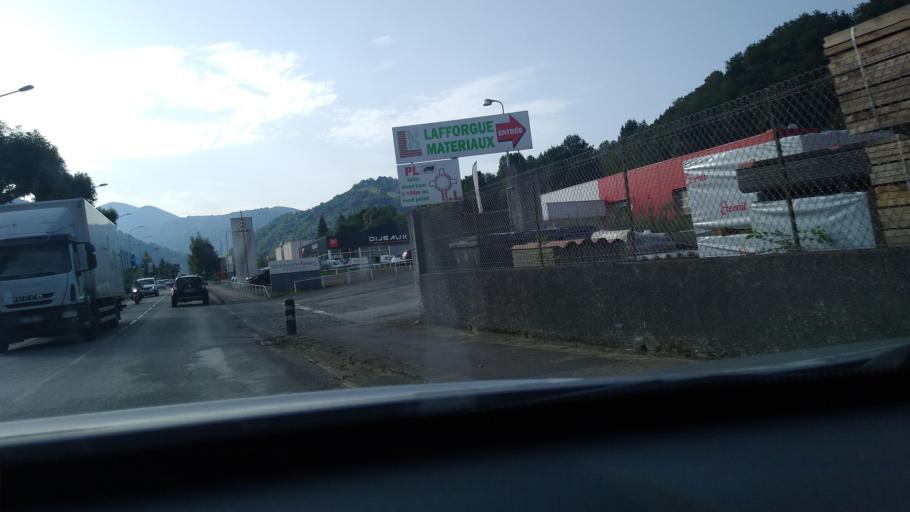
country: FR
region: Midi-Pyrenees
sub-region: Departement de l'Ariege
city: Saint-Girons
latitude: 42.9750
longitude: 1.1501
